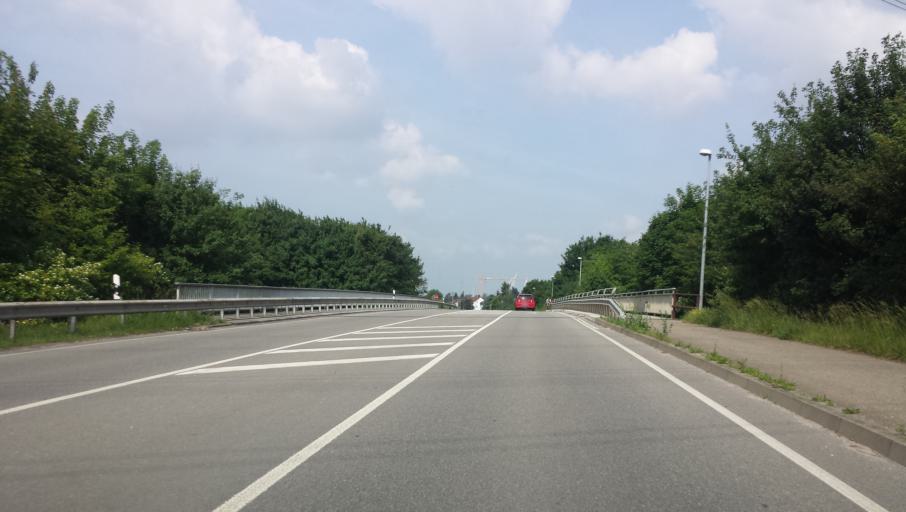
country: DE
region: Rheinland-Pfalz
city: Kuhardt
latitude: 49.1500
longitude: 8.3046
